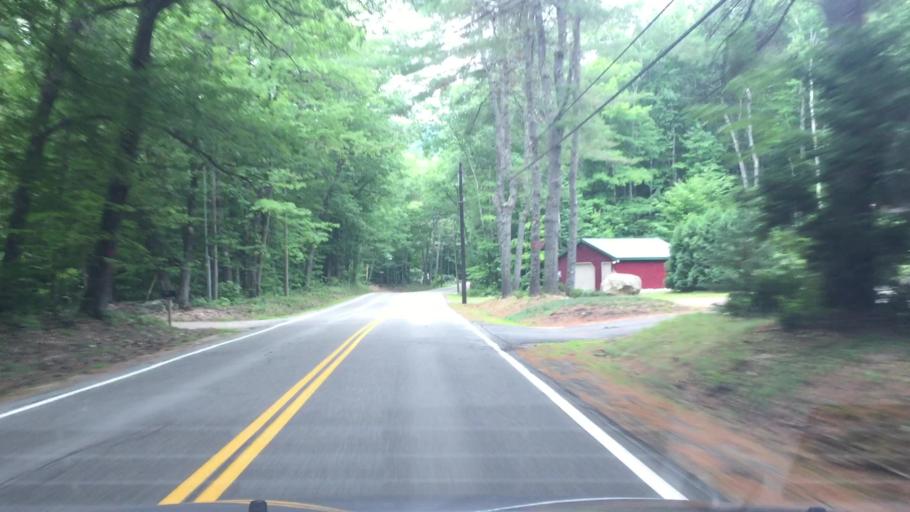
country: US
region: New Hampshire
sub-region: Carroll County
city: Madison
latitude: 43.8964
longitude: -71.0711
